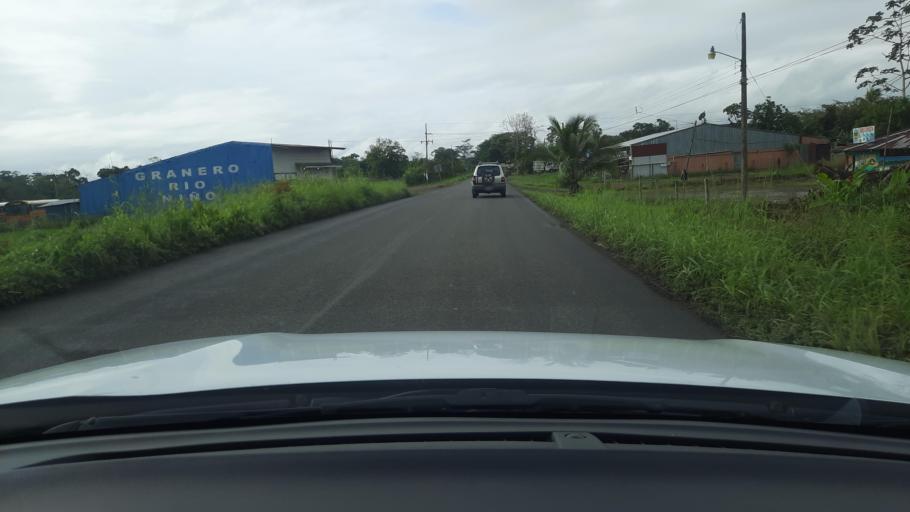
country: CR
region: Alajuela
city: San Jose
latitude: 10.9583
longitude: -85.1327
